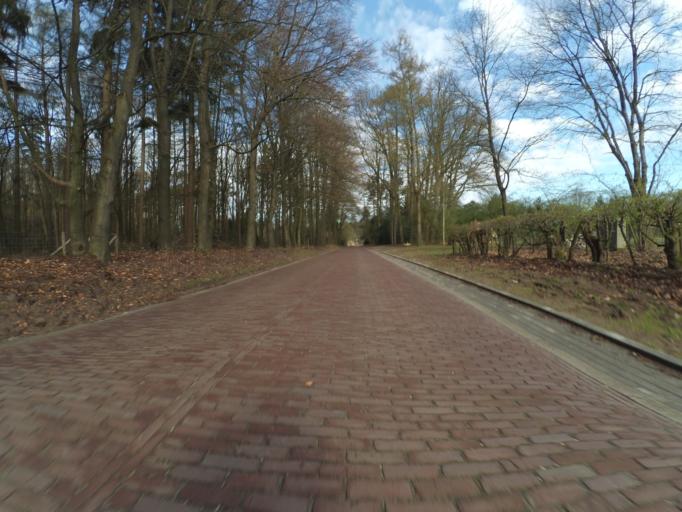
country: NL
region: Gelderland
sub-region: Gemeente Apeldoorn
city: Uddel
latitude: 52.1981
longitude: 5.8411
